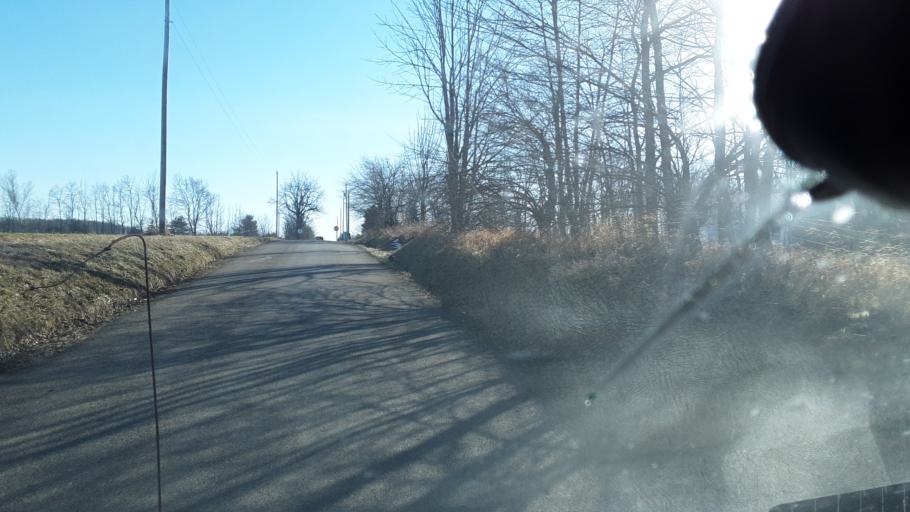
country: US
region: Ohio
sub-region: Ashland County
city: Loudonville
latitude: 40.7202
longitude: -82.2217
